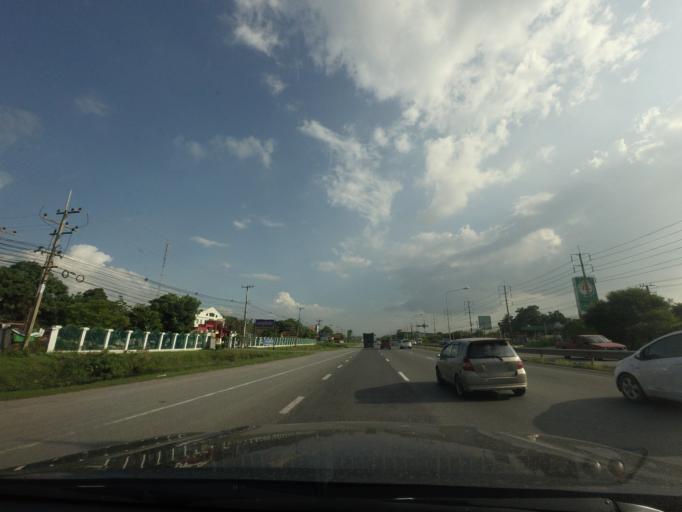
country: TH
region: Sara Buri
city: Chaloem Phra Kiat
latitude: 14.5735
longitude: 100.9024
